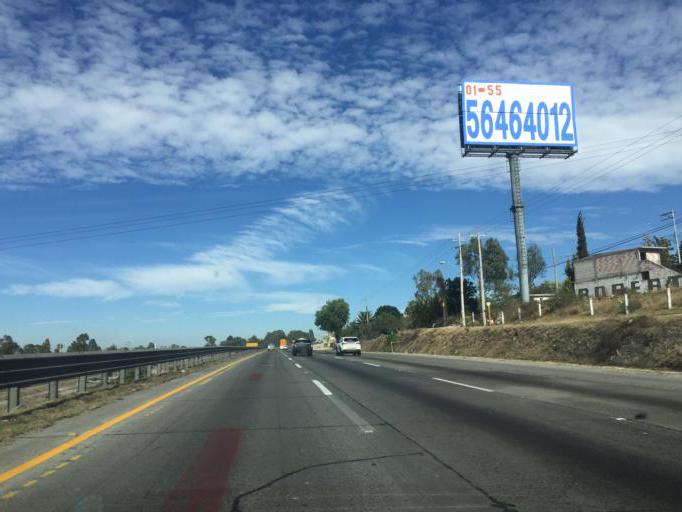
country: MX
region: Queretaro
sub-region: San Juan del Rio
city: Paso de Mata
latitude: 20.3384
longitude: -99.9426
